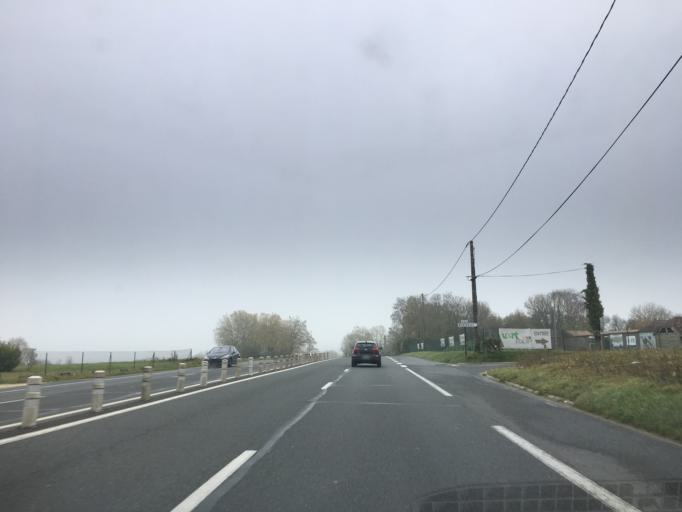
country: FR
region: Ile-de-France
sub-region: Departement de Seine-et-Marne
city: Vernou-la-Celle-sur-Seine
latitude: 48.3621
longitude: 2.8623
